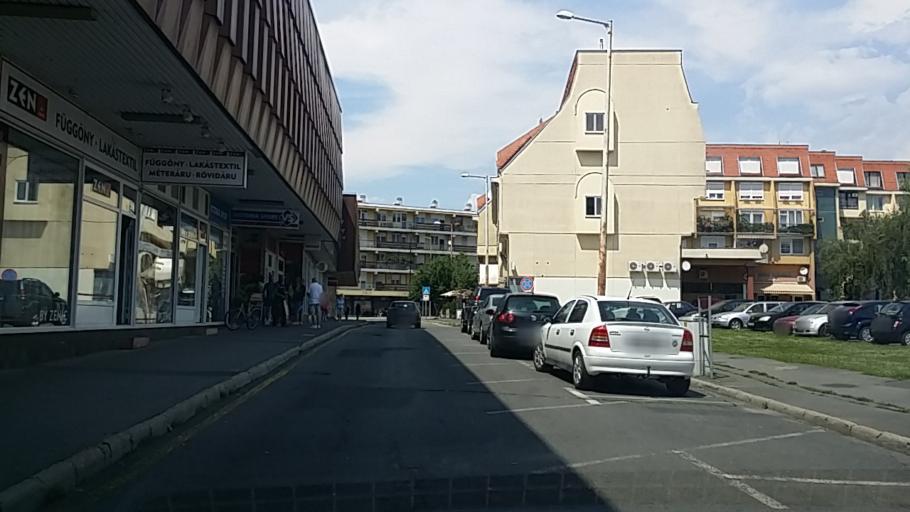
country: HU
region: Zala
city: Nagykanizsa
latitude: 46.4542
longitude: 16.9877
